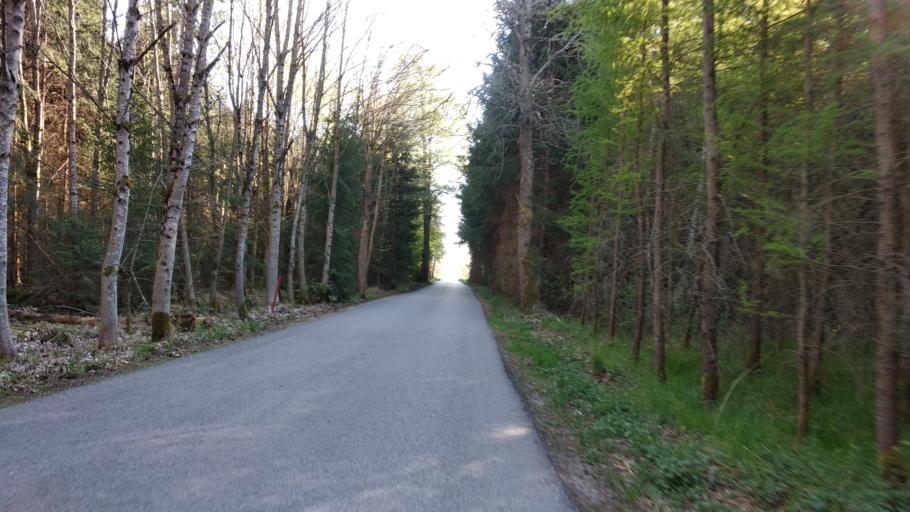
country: DE
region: Bavaria
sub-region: Upper Bavaria
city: Putzbrunn
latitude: 48.0609
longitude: 11.7198
